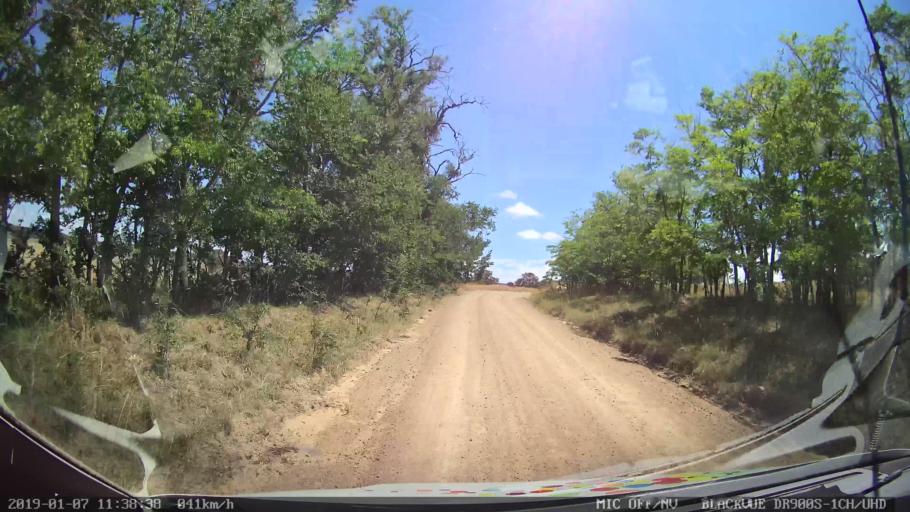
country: AU
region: New South Wales
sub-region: Armidale Dumaresq
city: Armidale
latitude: -30.3704
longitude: 151.5727
